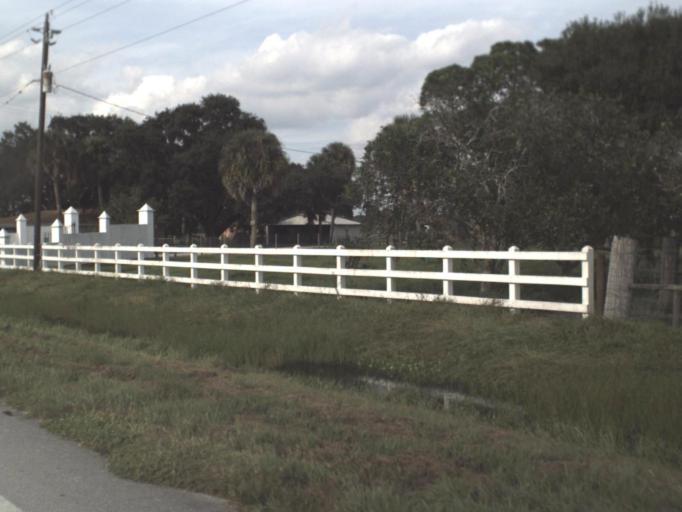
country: US
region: Florida
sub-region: Okeechobee County
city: Taylor Creek
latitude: 27.2321
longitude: -80.7750
